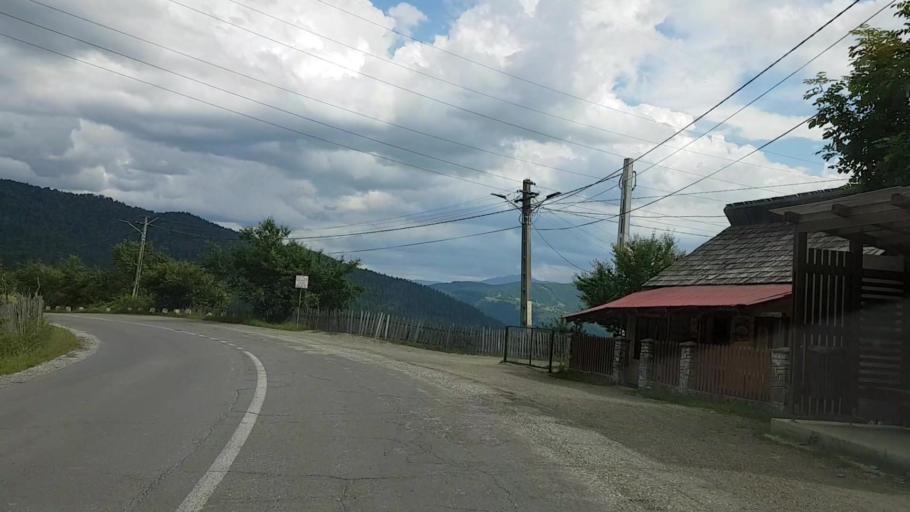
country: RO
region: Neamt
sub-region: Comuna Bicaz
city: Dodeni
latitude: 46.9871
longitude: 26.1019
